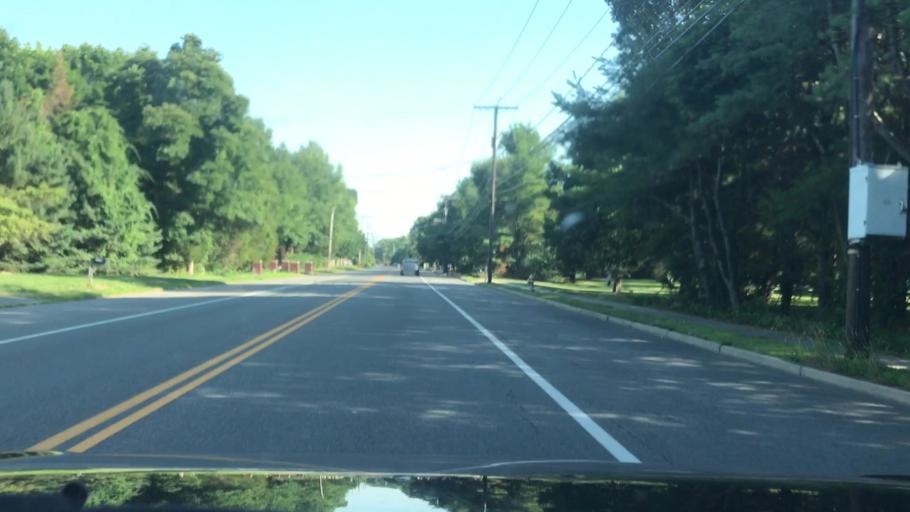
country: US
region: New Jersey
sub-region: Ocean County
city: Leisure Village
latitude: 40.0248
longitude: -74.2006
